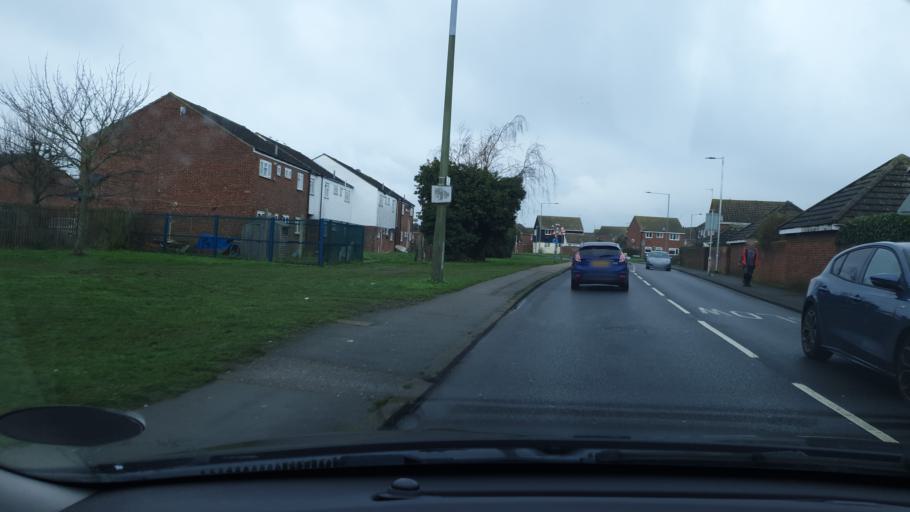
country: GB
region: England
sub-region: Essex
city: Clacton-on-Sea
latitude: 51.7977
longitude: 1.1320
